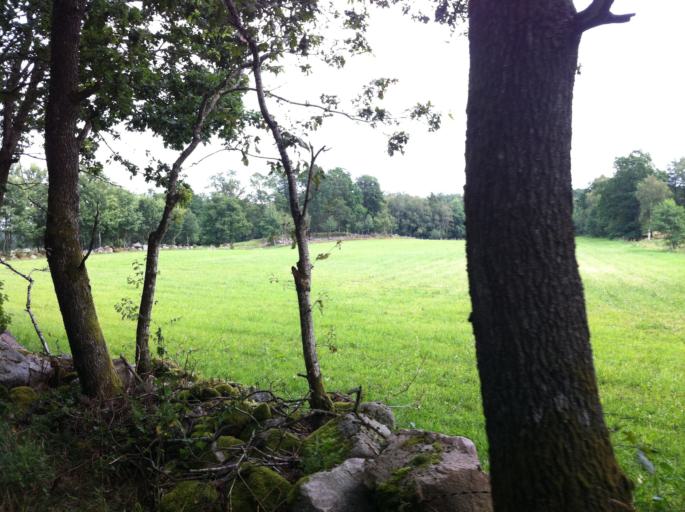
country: SE
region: Skane
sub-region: Horby Kommun
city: Hoerby
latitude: 55.9216
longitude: 13.8045
